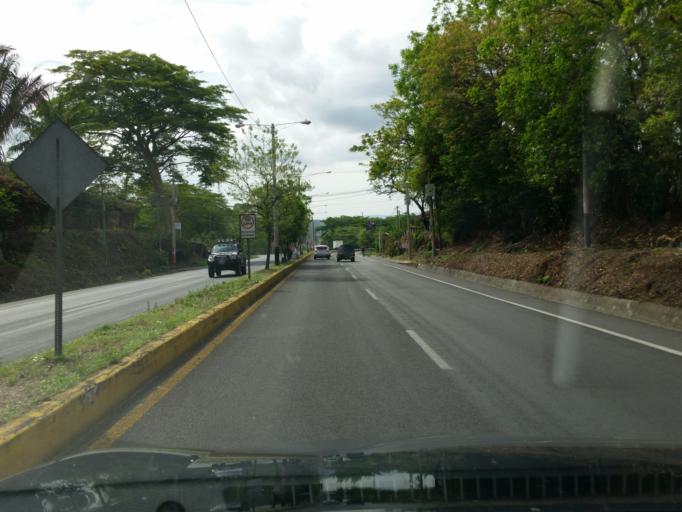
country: NI
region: Masaya
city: Ticuantepe
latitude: 12.0278
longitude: -86.1776
